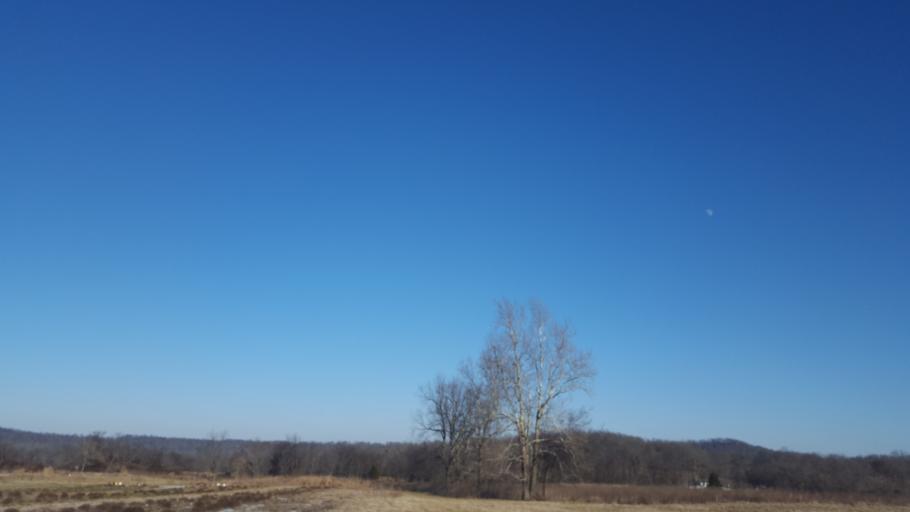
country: US
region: Kentucky
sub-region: Crittenden County
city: Marion
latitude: 37.4346
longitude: -88.0487
